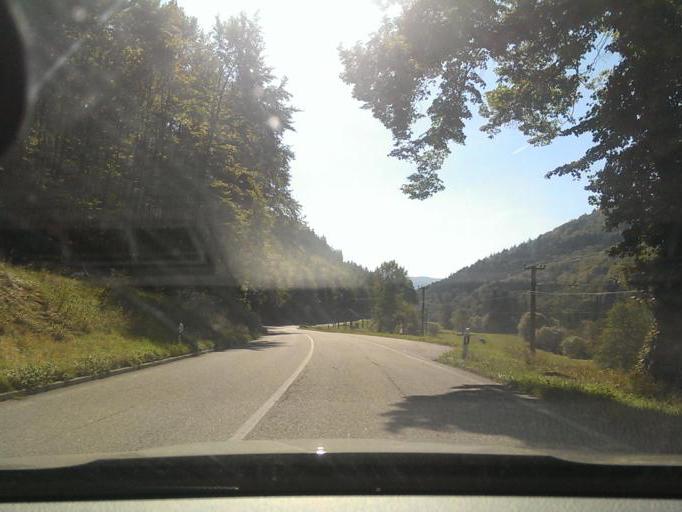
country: DE
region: Baden-Wuerttemberg
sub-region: Karlsruhe Region
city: Bad Herrenalb
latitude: 48.8325
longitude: 8.4428
